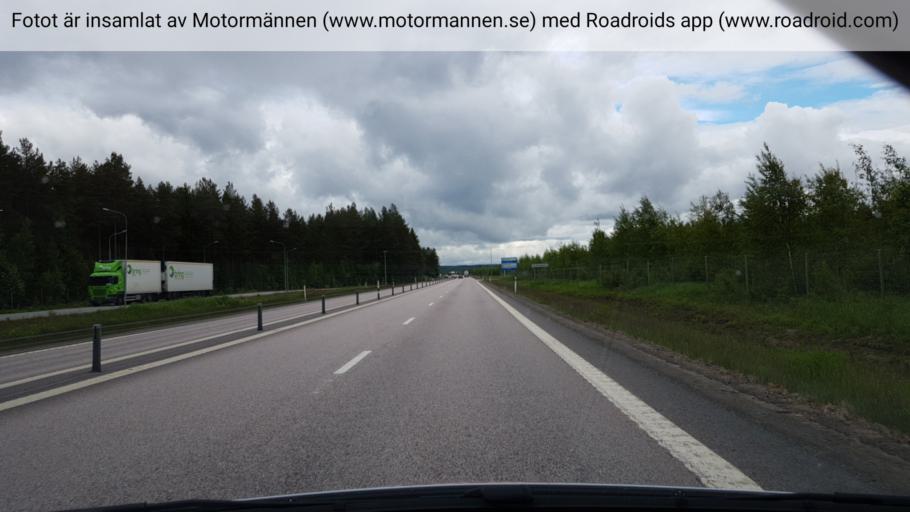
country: SE
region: Vaesterbotten
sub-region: Nordmalings Kommun
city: Nordmaling
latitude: 63.5523
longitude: 19.4178
